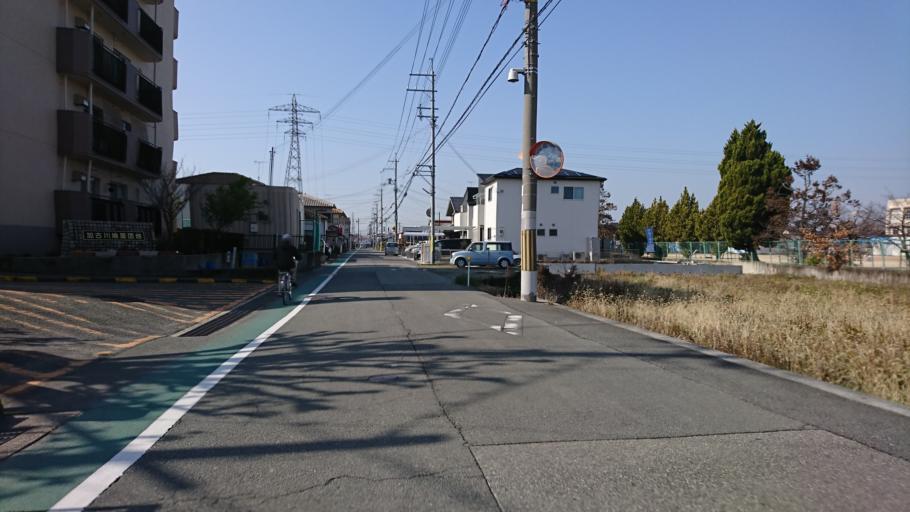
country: JP
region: Hyogo
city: Kakogawacho-honmachi
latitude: 34.7601
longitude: 134.8220
